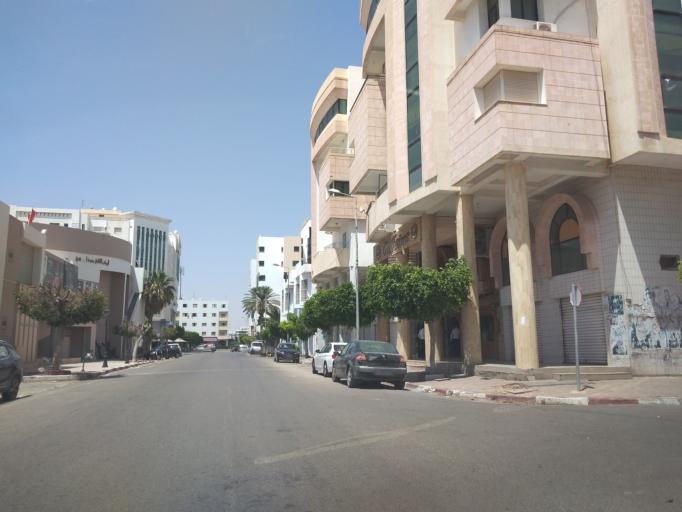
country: TN
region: Safaqis
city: Sfax
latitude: 34.7365
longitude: 10.7514
